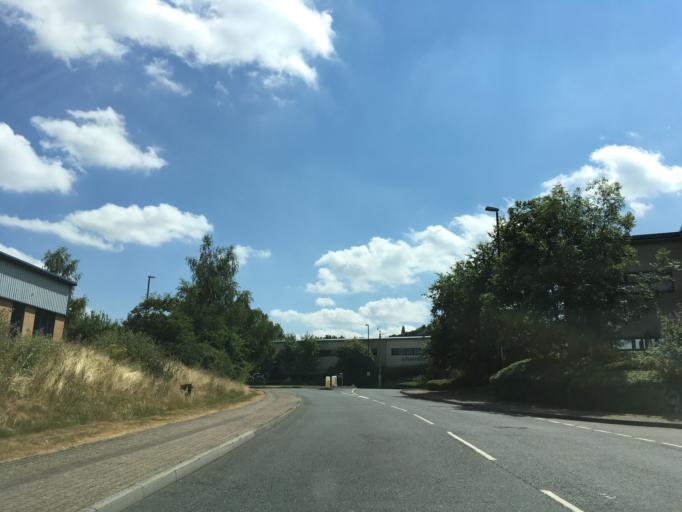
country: GB
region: England
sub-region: Gloucestershire
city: Churchdown
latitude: 51.8396
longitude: -2.1673
